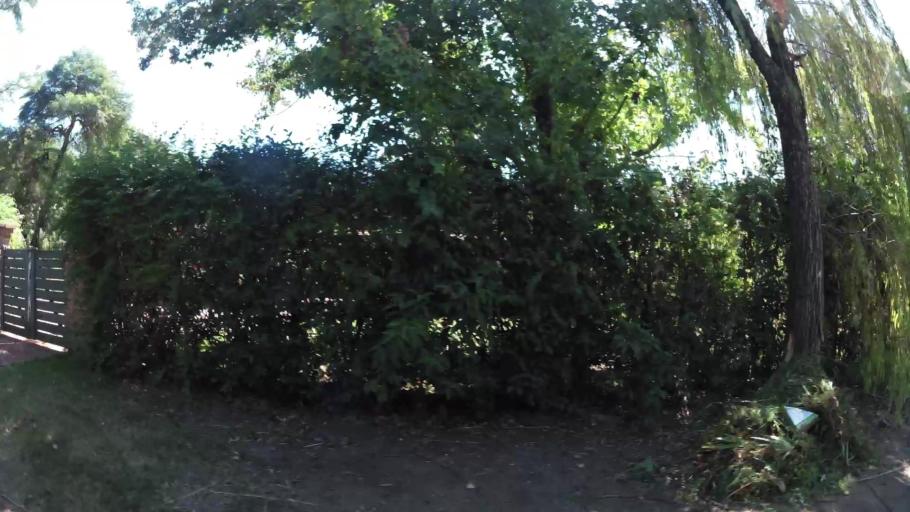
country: AR
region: Cordoba
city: Villa Allende
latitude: -31.2811
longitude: -64.2934
